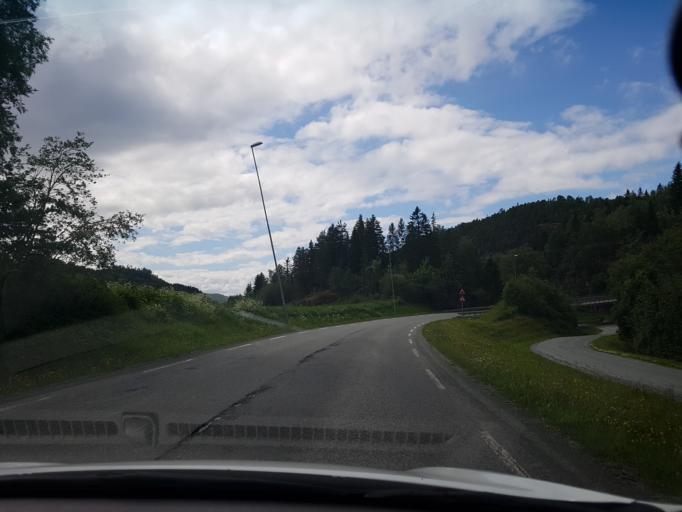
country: NO
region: Nord-Trondelag
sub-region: Stjordal
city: Stjordalshalsen
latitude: 63.6019
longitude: 10.9643
